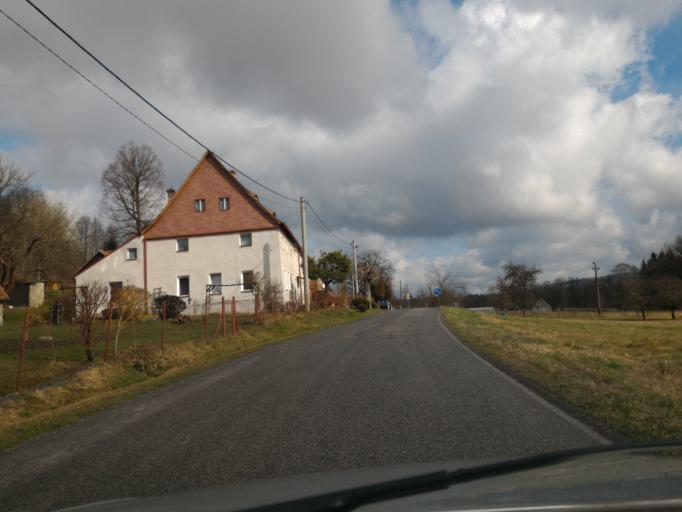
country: CZ
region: Liberecky
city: Visnova
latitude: 50.9904
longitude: 15.0217
